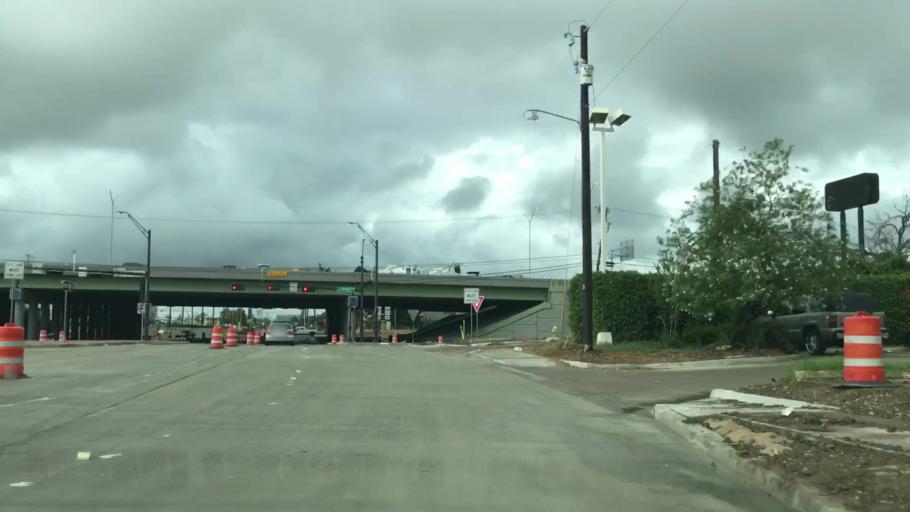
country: US
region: Texas
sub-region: Dallas County
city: Irving
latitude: 32.8359
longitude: -96.9302
